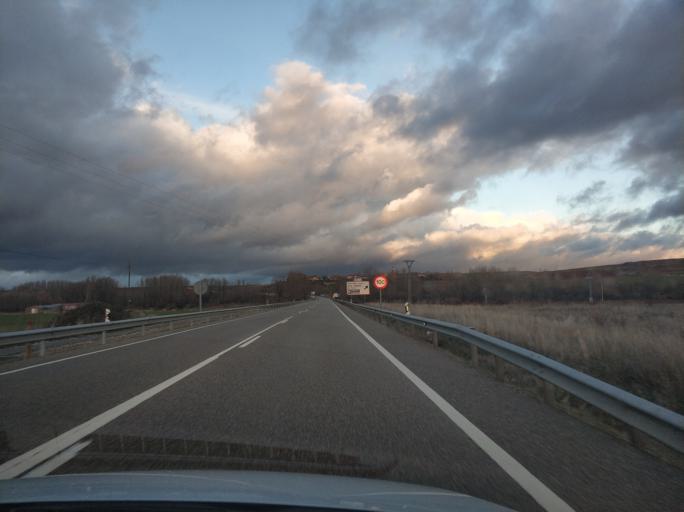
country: ES
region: Castille and Leon
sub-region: Provincia de Segovia
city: Ayllon
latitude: 41.4092
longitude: -3.4139
